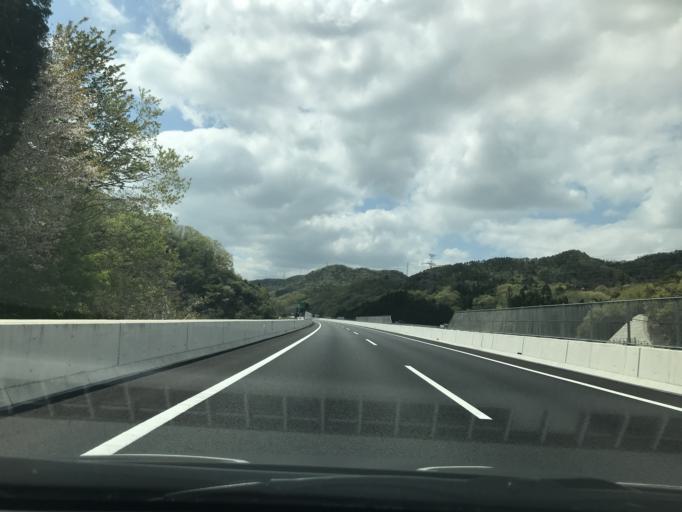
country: JP
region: Hyogo
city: Takarazuka
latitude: 34.8880
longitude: 135.3550
